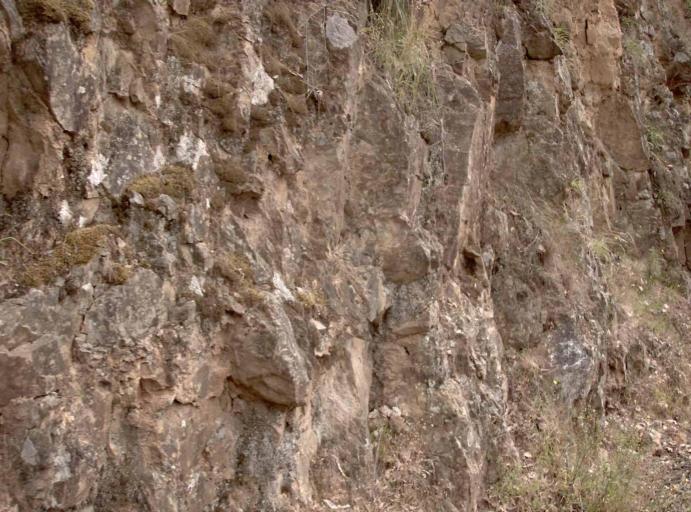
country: AU
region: Victoria
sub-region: Wellington
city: Heyfield
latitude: -37.7377
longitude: 146.6707
